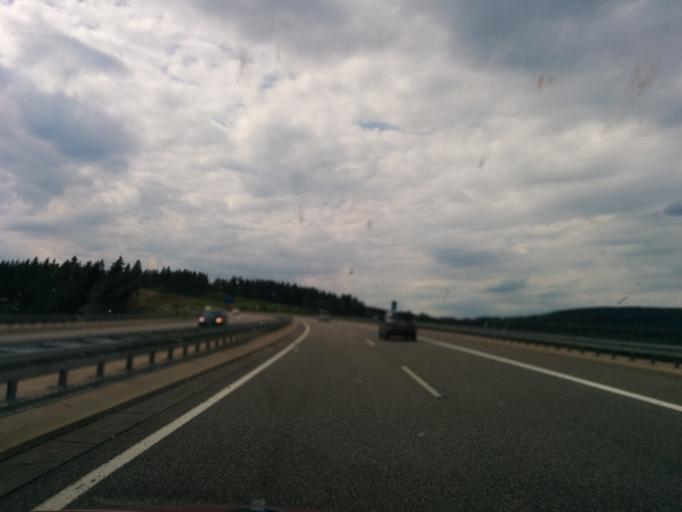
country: DE
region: Thuringia
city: Suhl
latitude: 50.5725
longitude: 10.7286
